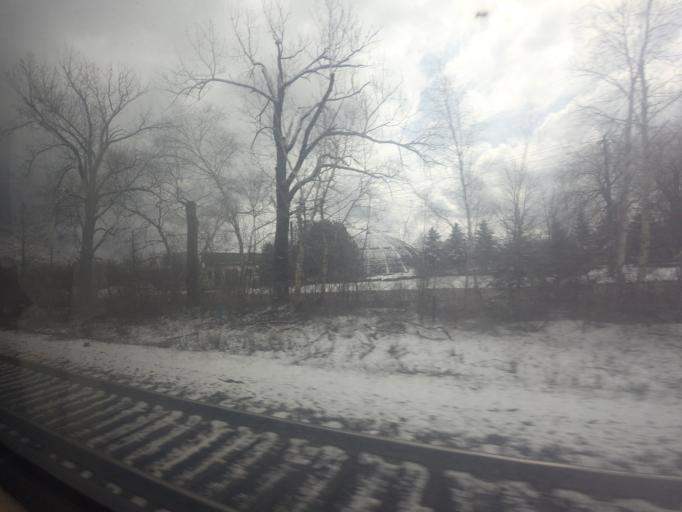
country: CA
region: Ontario
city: Scarborough
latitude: 43.7607
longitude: -79.1683
